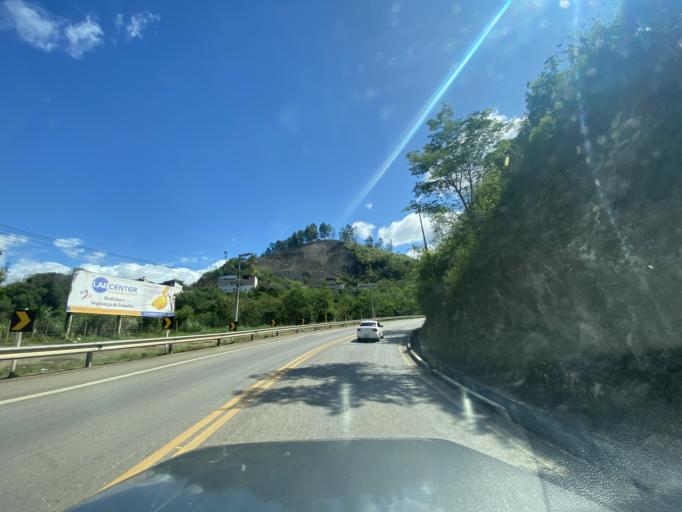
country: BR
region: Espirito Santo
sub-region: Alegre
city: Alegre
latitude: -20.7620
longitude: -41.5214
